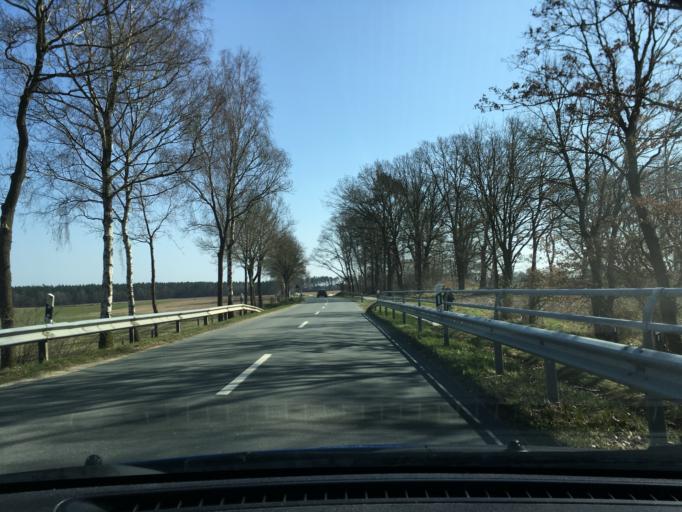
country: DE
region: Lower Saxony
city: Wriedel
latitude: 53.0048
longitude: 10.2925
